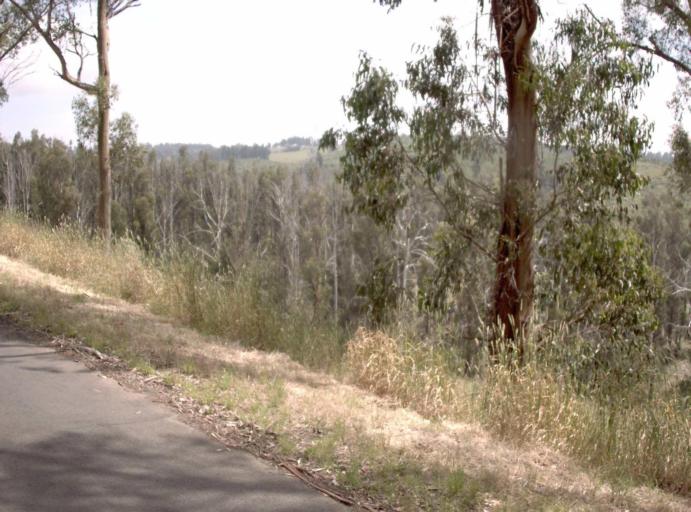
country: AU
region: Victoria
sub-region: Latrobe
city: Traralgon
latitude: -38.3220
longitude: 146.5695
